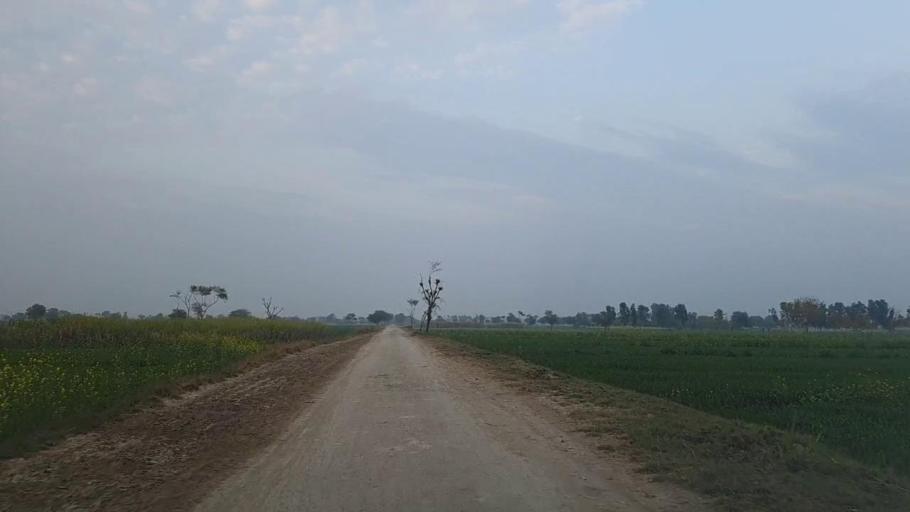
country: PK
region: Sindh
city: Jam Sahib
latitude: 26.2930
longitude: 68.5934
